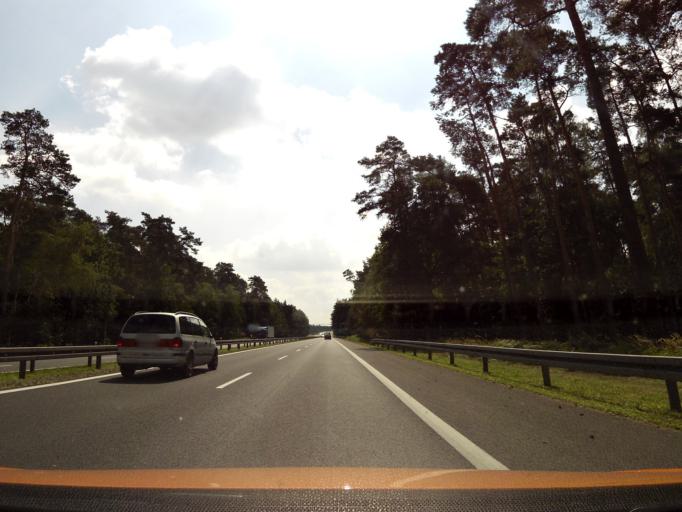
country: PL
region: West Pomeranian Voivodeship
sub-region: Powiat goleniowski
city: Goleniow
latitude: 53.5421
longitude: 14.8044
